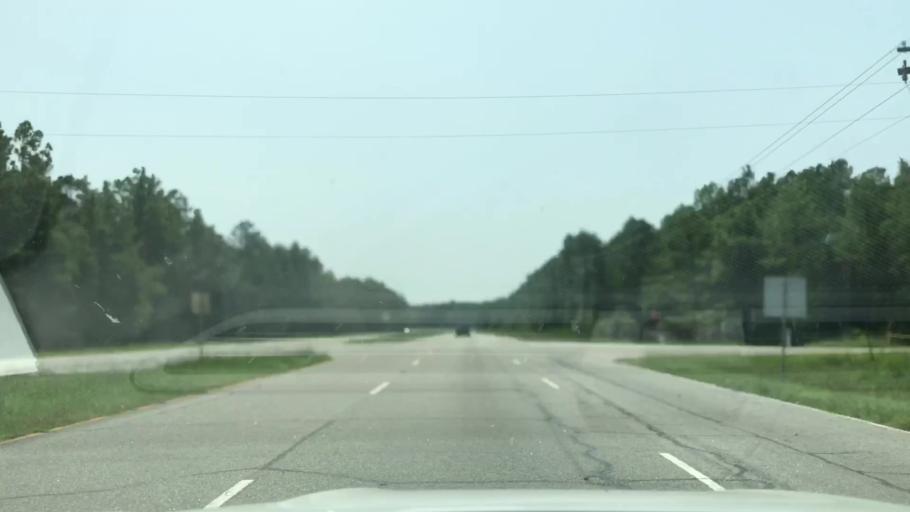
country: US
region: South Carolina
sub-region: Georgetown County
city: Georgetown
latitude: 33.2991
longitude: -79.3426
